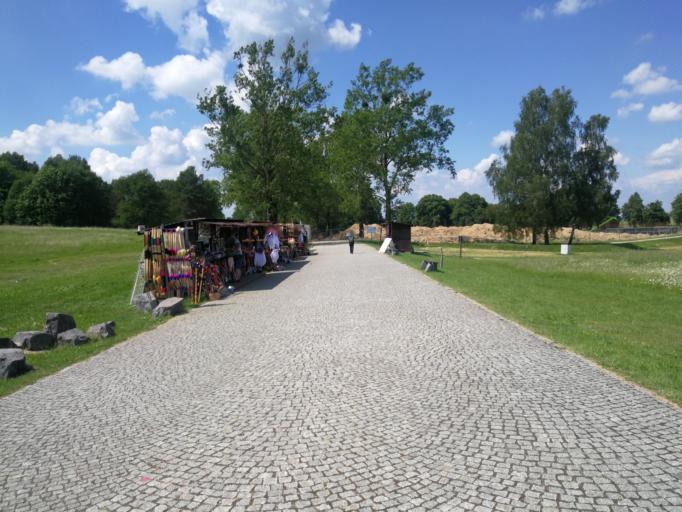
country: PL
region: Warmian-Masurian Voivodeship
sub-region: Powiat ostrodzki
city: Gierzwald
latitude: 53.4882
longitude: 20.1205
